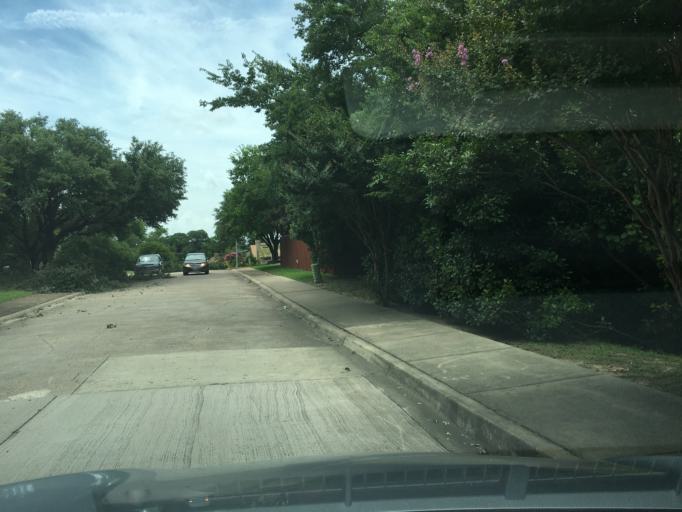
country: US
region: Texas
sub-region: Dallas County
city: Richardson
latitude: 32.9120
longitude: -96.7152
